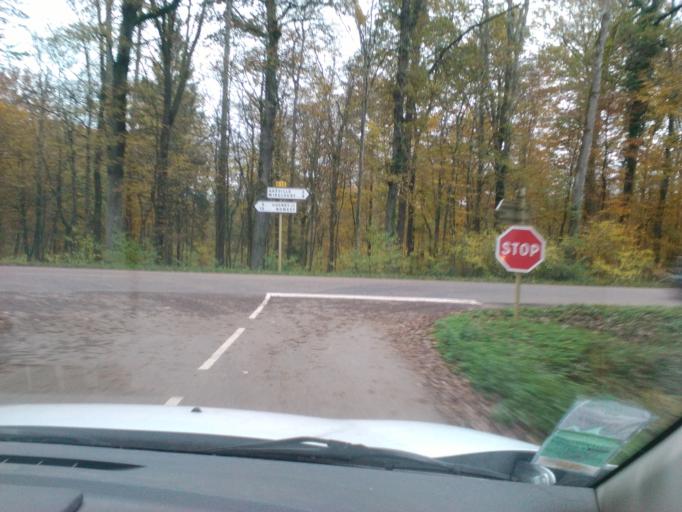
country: FR
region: Lorraine
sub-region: Departement des Vosges
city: Mirecourt
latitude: 48.2968
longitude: 6.2128
